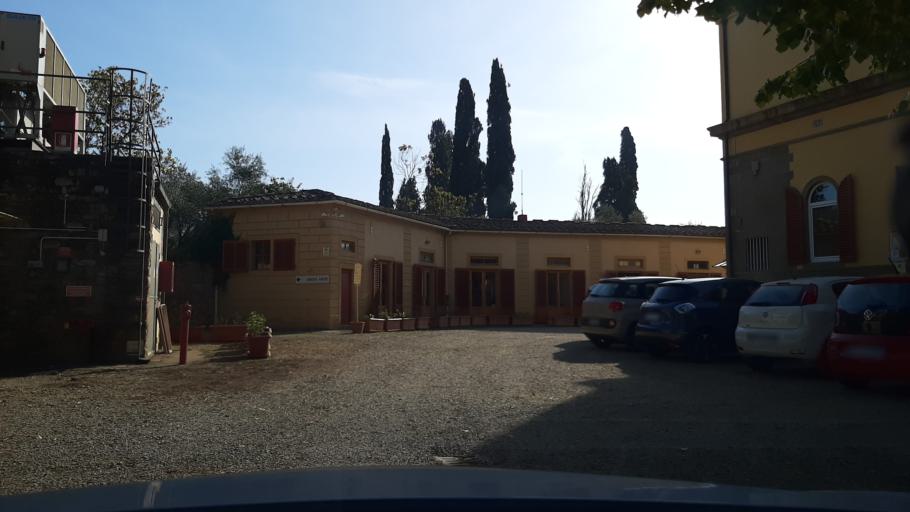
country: IT
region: Tuscany
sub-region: Province of Florence
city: Florence
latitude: 43.7508
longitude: 11.2544
